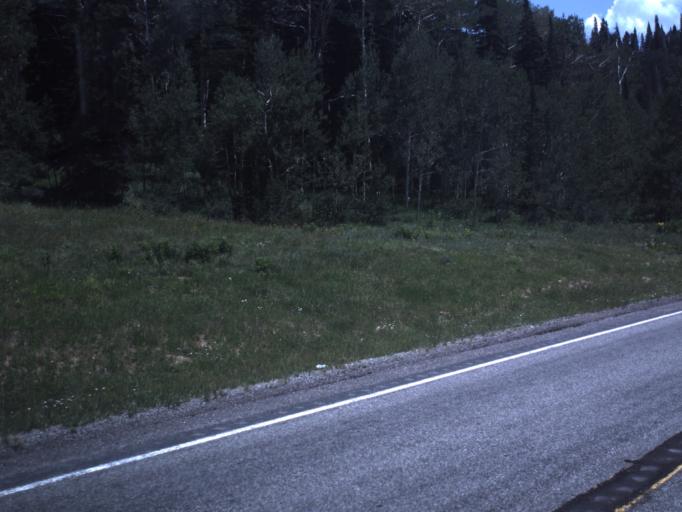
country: US
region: Utah
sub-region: Sanpete County
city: Fairview
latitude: 39.6056
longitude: -111.2767
